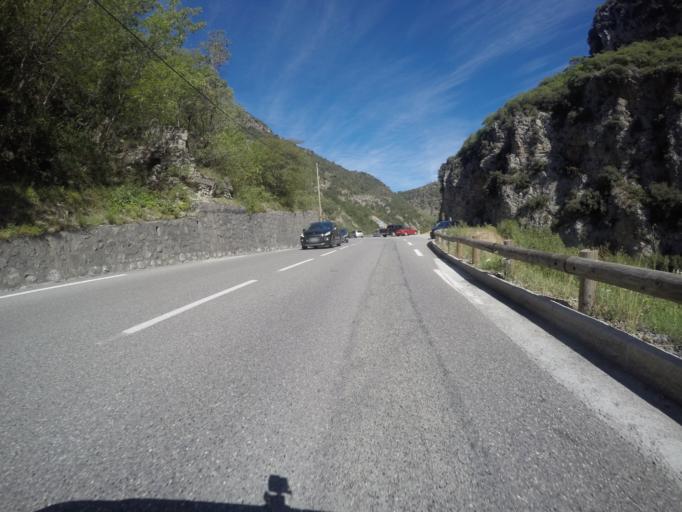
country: FR
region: Provence-Alpes-Cote d'Azur
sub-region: Departement des Alpes-Maritimes
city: Gilette
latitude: 43.9311
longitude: 7.1763
